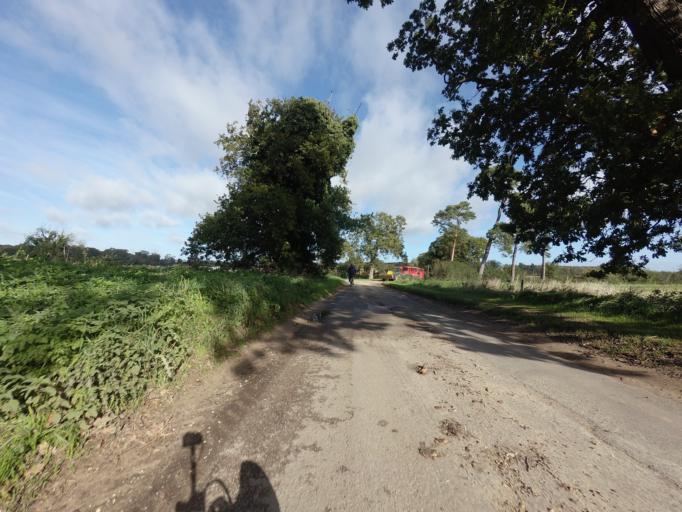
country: GB
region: England
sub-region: Norfolk
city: Dersingham
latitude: 52.8617
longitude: 0.6659
